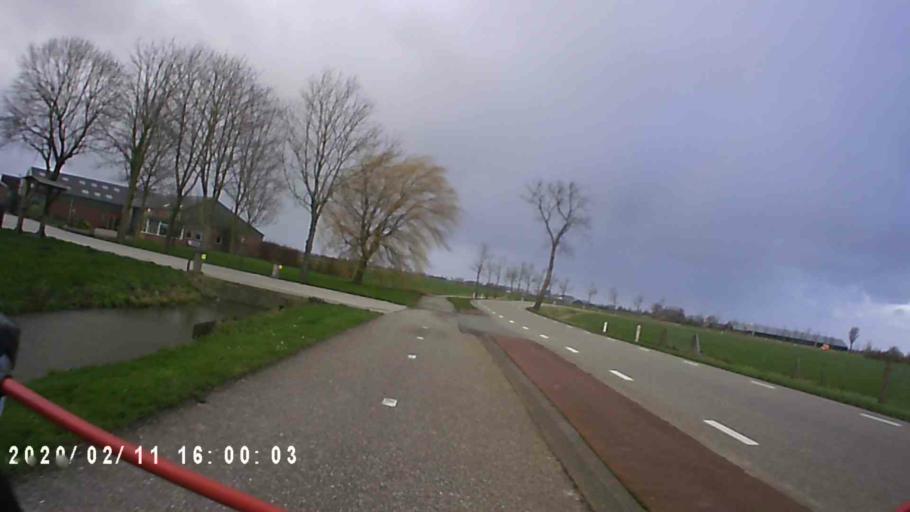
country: NL
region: Groningen
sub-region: Gemeente Zuidhorn
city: Oldehove
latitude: 53.2923
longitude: 6.4215
